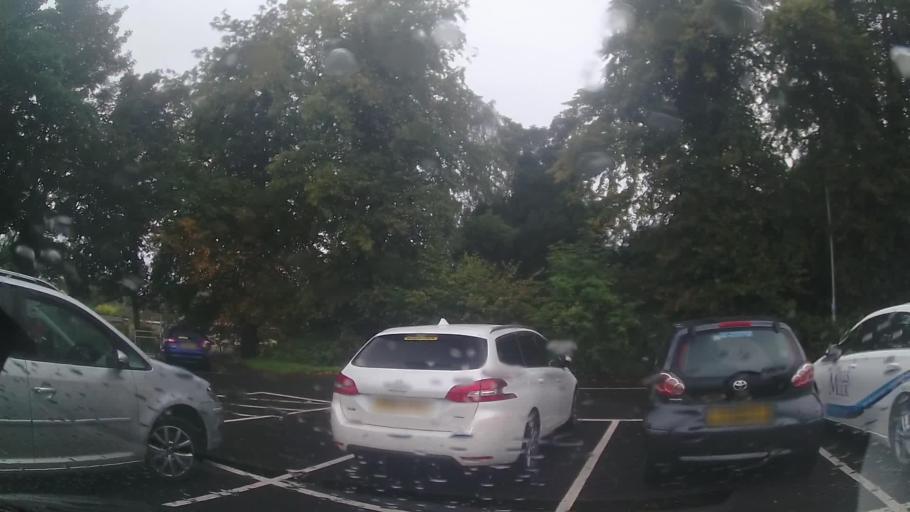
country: GB
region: Scotland
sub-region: East Ayrshire
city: Mauchline
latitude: 55.5155
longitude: -4.3820
